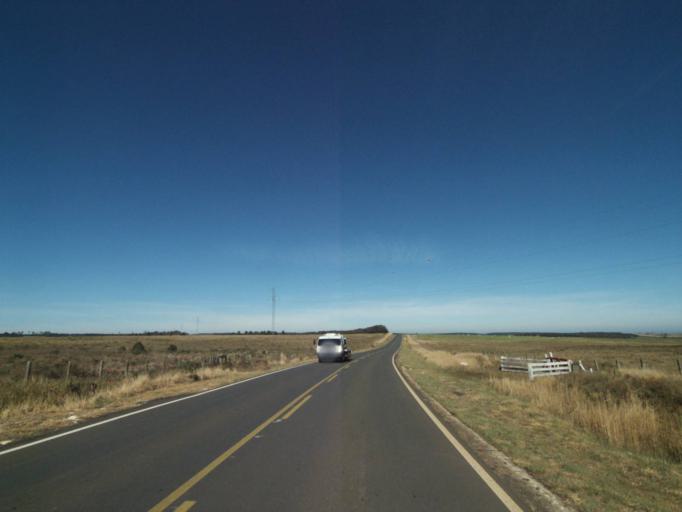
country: BR
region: Parana
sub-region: Castro
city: Castro
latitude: -24.6783
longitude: -50.2131
